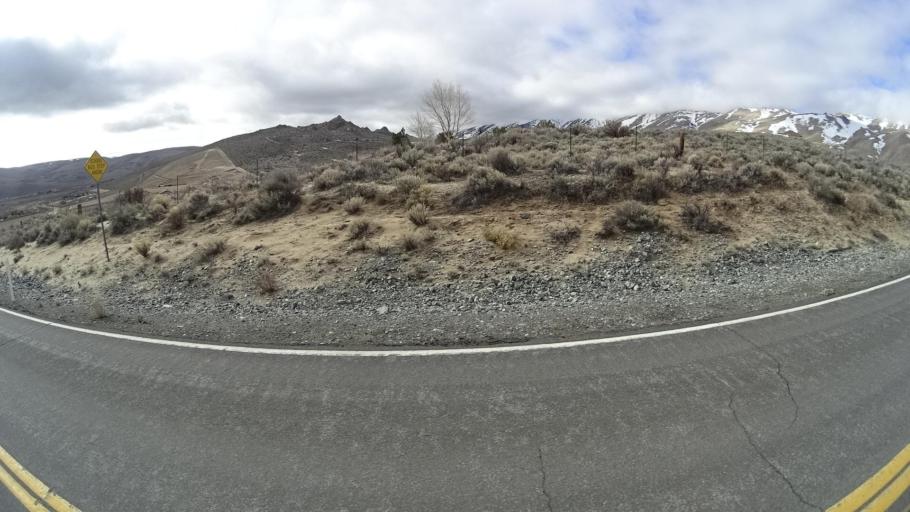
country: US
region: Nevada
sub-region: Washoe County
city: Cold Springs
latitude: 39.8673
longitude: -119.9462
